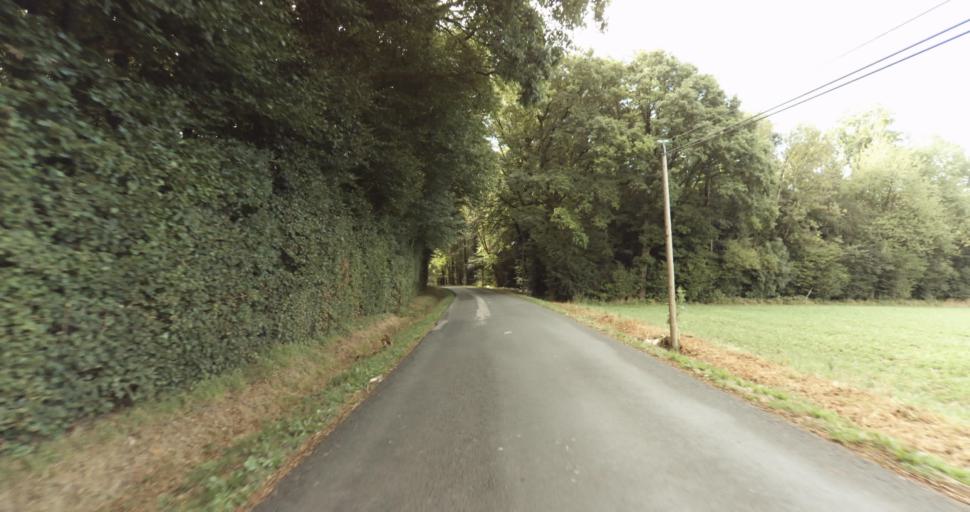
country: FR
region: Lower Normandy
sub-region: Departement de l'Orne
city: Gace
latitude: 48.8146
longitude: 0.2373
